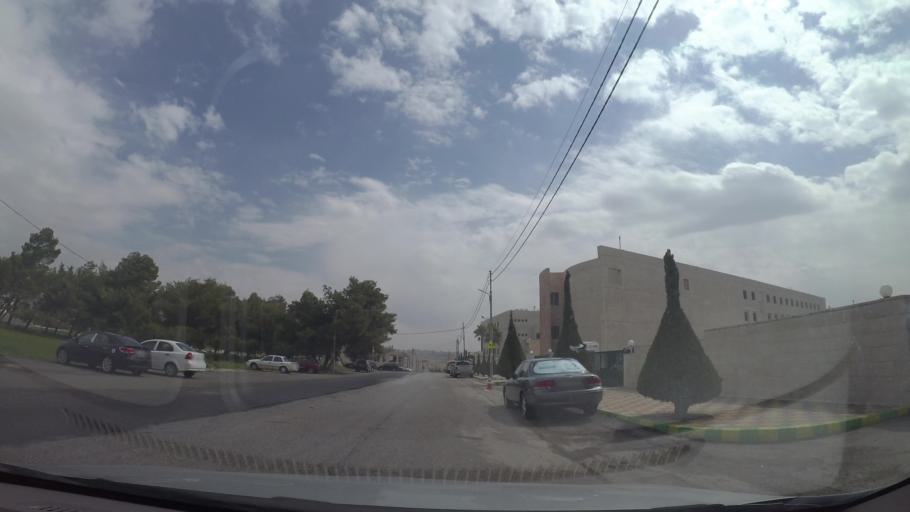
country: JO
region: Amman
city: Umm as Summaq
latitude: 31.9118
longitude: 35.8526
